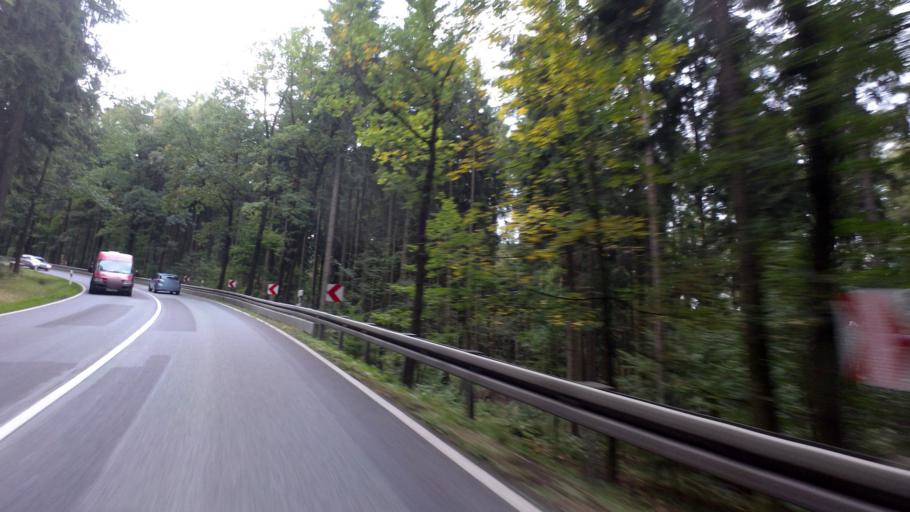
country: DE
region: Saxony
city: Oppach
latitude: 51.0776
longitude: 14.4873
